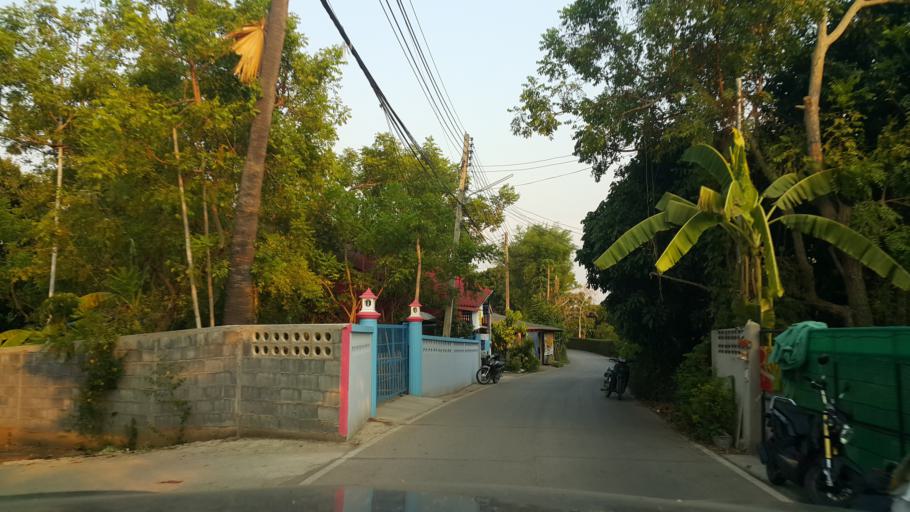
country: TH
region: Chiang Mai
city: Saraphi
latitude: 18.7190
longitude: 99.0241
